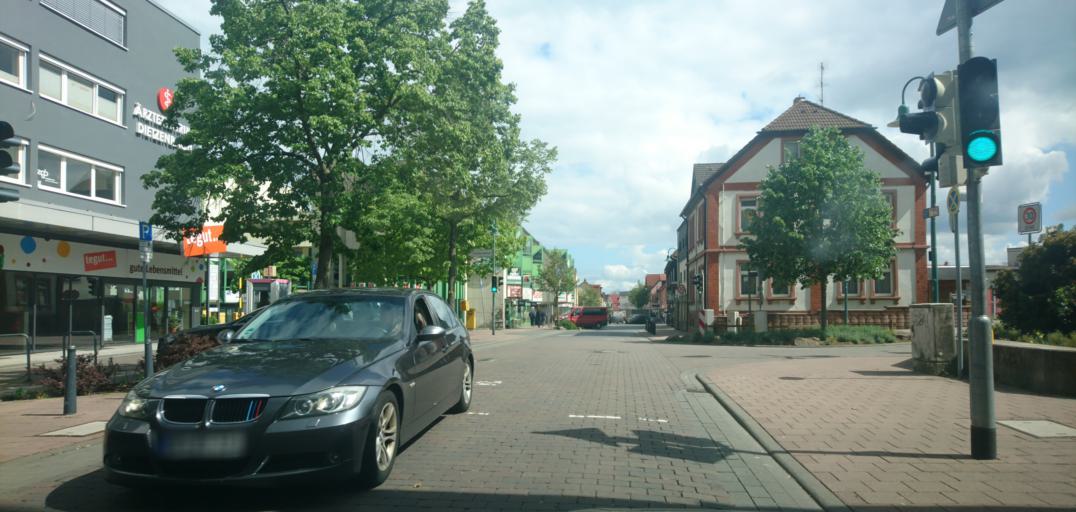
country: DE
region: Hesse
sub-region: Regierungsbezirk Darmstadt
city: Dietzenbach
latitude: 50.0099
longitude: 8.7791
